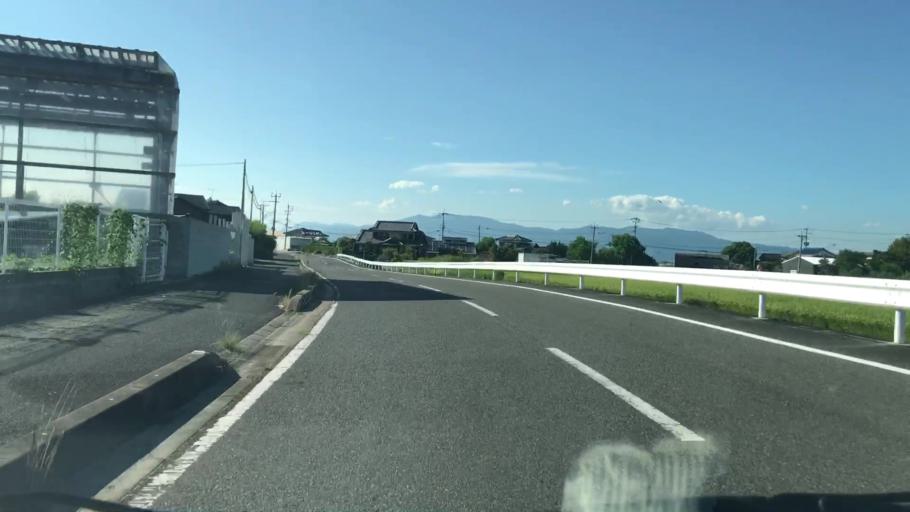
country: JP
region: Saga Prefecture
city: Saga-shi
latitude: 33.1888
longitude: 130.2890
